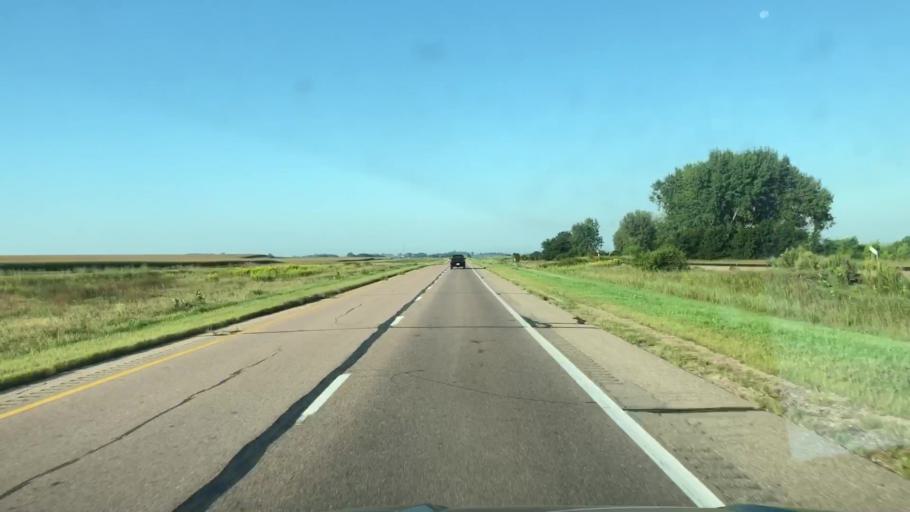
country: US
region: Iowa
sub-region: Sioux County
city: Alton
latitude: 43.0252
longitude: -95.9437
